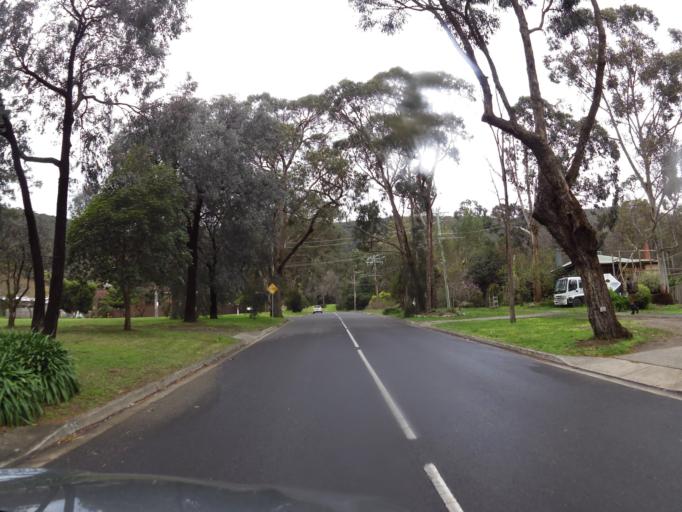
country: AU
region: Victoria
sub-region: Knox
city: Ferntree Gully
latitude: -37.8748
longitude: 145.3053
